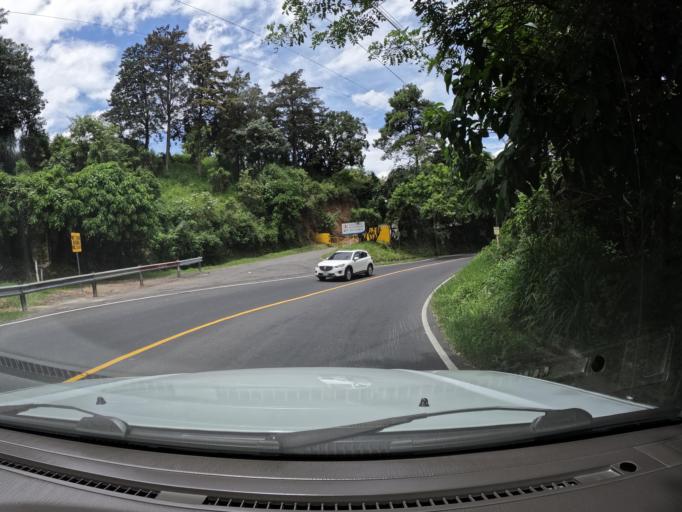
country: GT
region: Guatemala
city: Amatitlan
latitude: 14.4970
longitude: -90.6245
